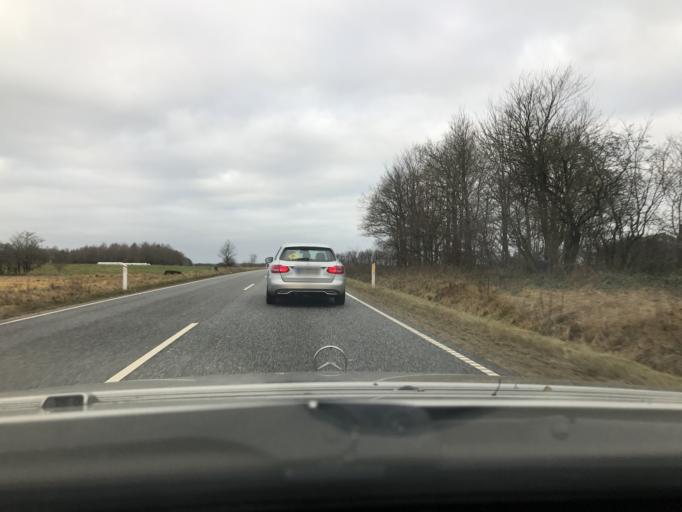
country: DK
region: South Denmark
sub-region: Tonder Kommune
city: Toftlund
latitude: 55.1207
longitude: 9.1547
